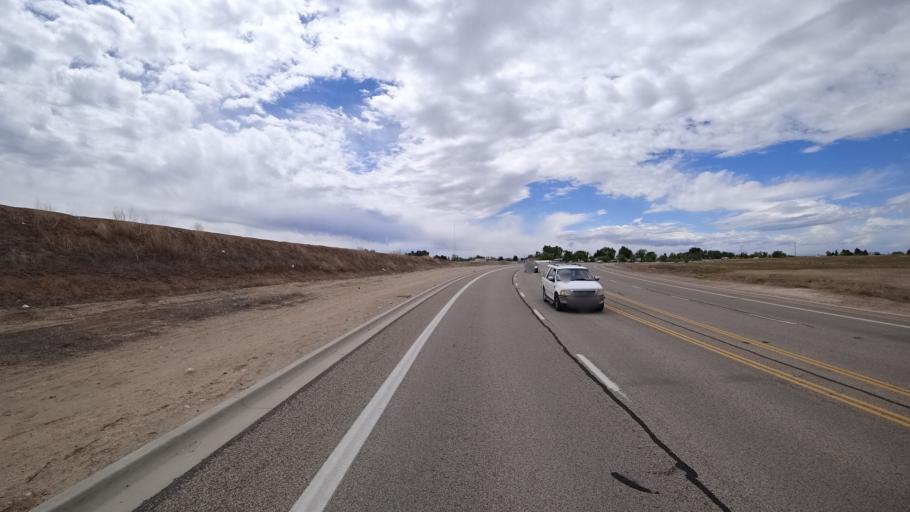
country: US
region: Idaho
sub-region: Ada County
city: Meridian
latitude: 43.5860
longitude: -116.4290
